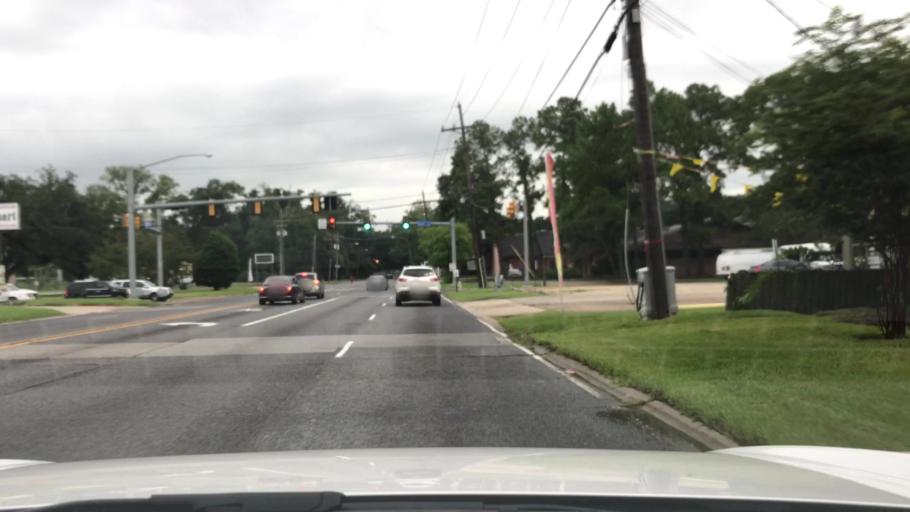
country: US
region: Louisiana
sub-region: East Baton Rouge Parish
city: Baton Rouge
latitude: 30.4534
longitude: -91.1390
